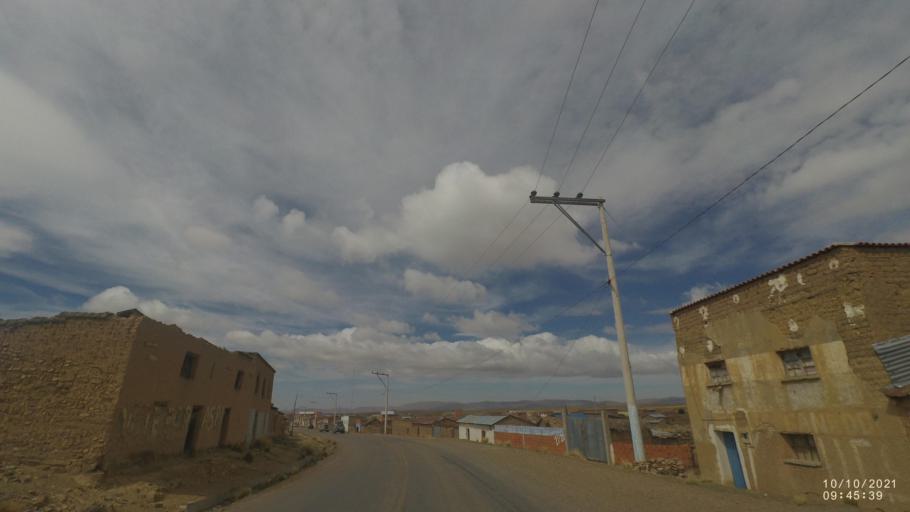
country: BO
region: La Paz
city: Quime
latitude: -17.1732
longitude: -67.3370
